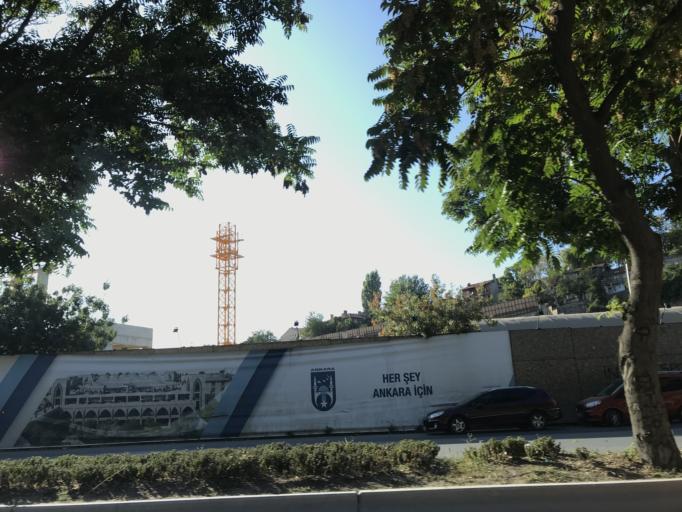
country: TR
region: Ankara
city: Ankara
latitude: 39.9463
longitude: 32.8609
